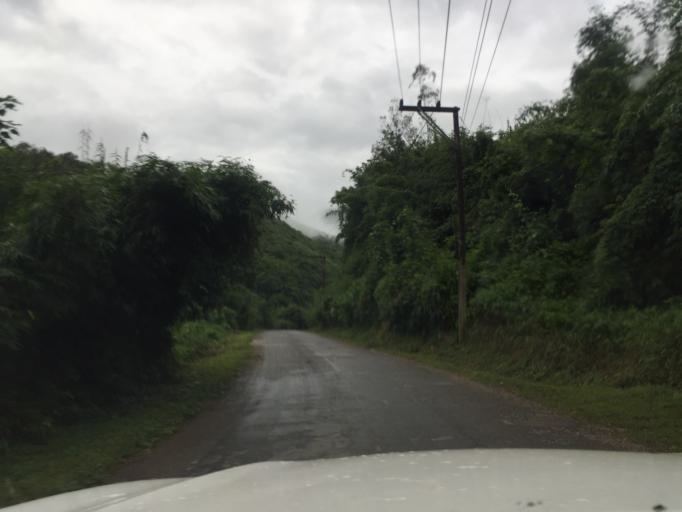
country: LA
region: Oudomxai
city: Muang La
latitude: 20.9303
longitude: 102.2064
